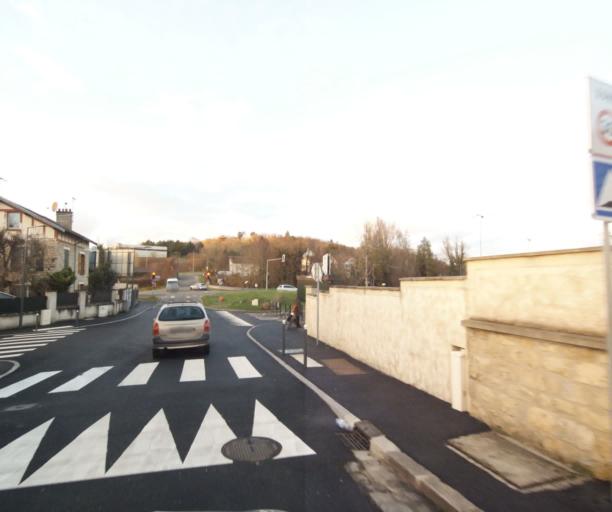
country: FR
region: Ile-de-France
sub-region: Departement des Yvelines
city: Meulan-en-Yvelines
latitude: 49.0115
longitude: 1.9079
